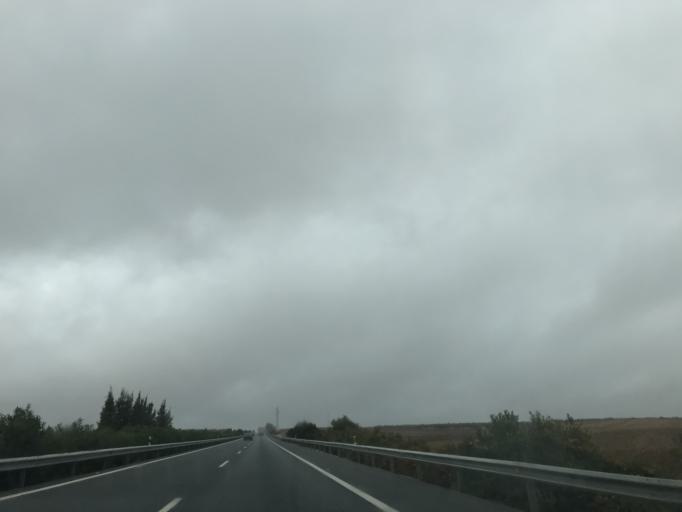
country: ES
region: Andalusia
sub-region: Provincia de Malaga
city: Fuente de Piedra
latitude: 37.1598
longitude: -4.7503
